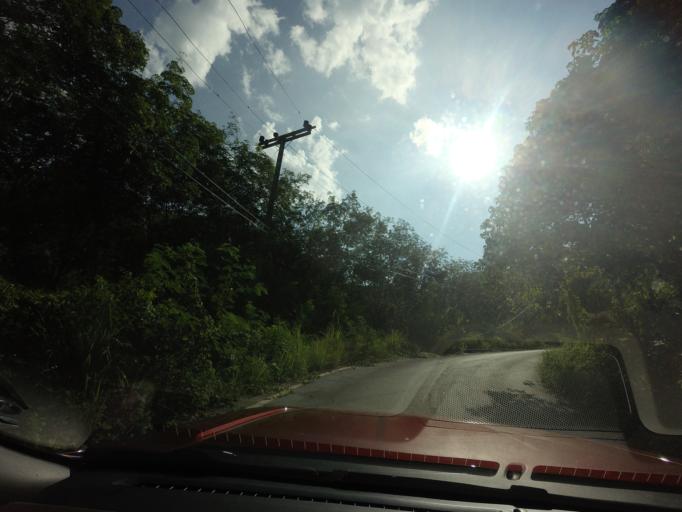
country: TH
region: Yala
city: Than To
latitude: 6.0643
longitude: 101.3612
